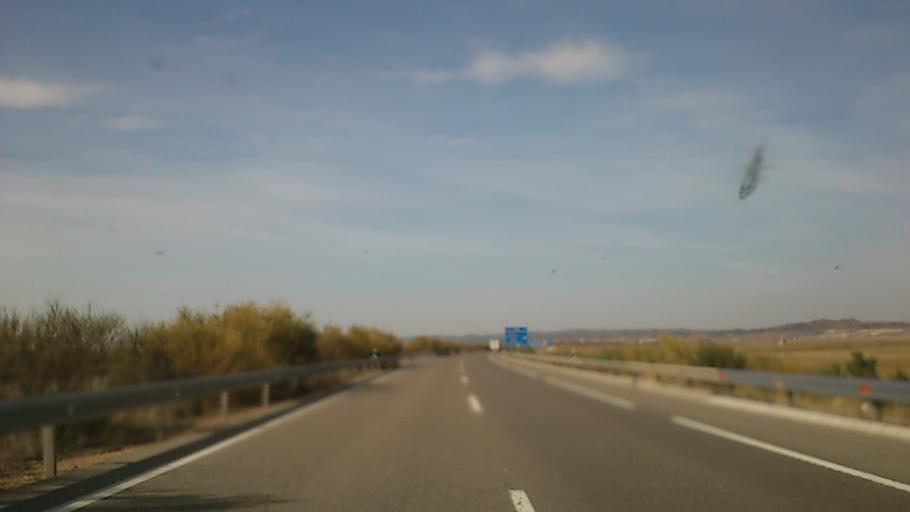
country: ES
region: Aragon
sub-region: Provincia de Teruel
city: Fuentes Claras
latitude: 40.8726
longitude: -1.3072
